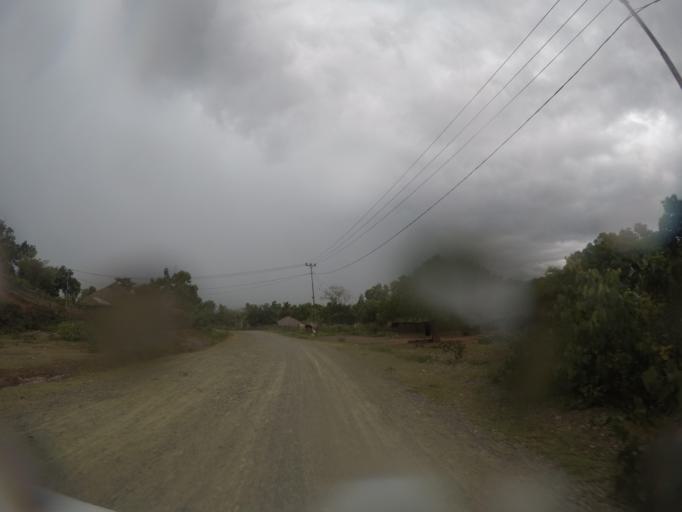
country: TL
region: Bobonaro
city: Maliana
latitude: -8.8537
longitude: 125.0861
